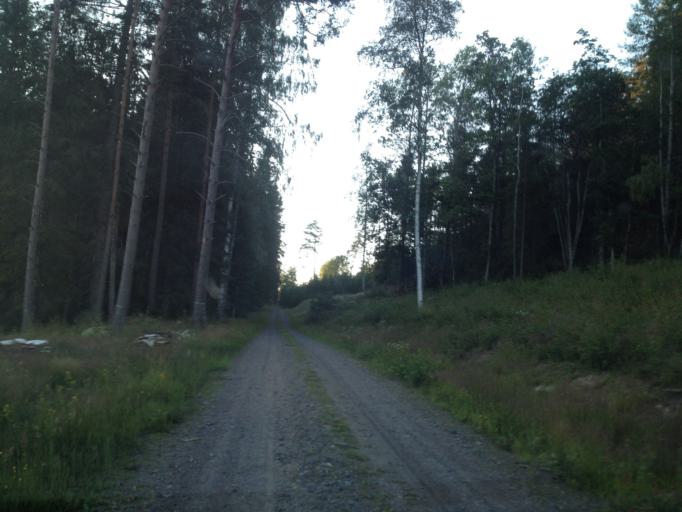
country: SE
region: Kalmar
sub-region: Vasterviks Kommun
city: Overum
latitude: 58.0094
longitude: 16.1222
